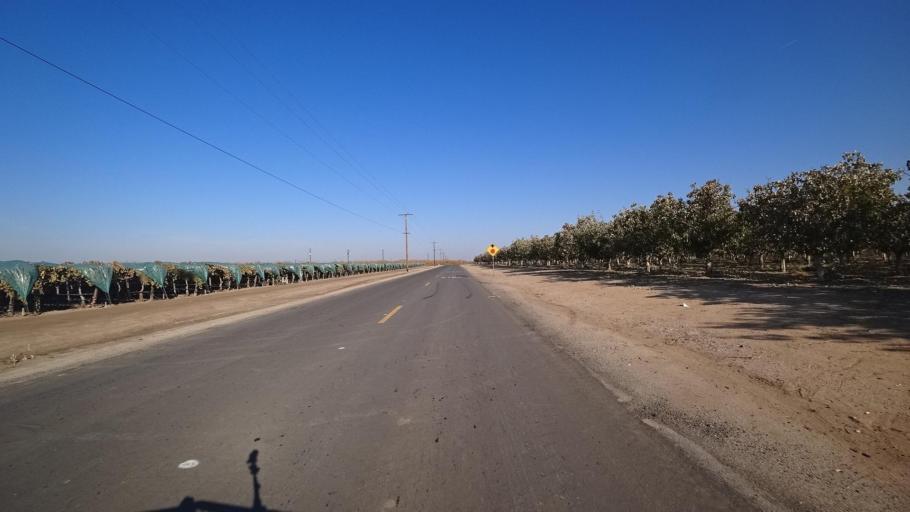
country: US
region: California
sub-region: Tulare County
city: Richgrove
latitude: 35.7569
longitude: -119.1340
